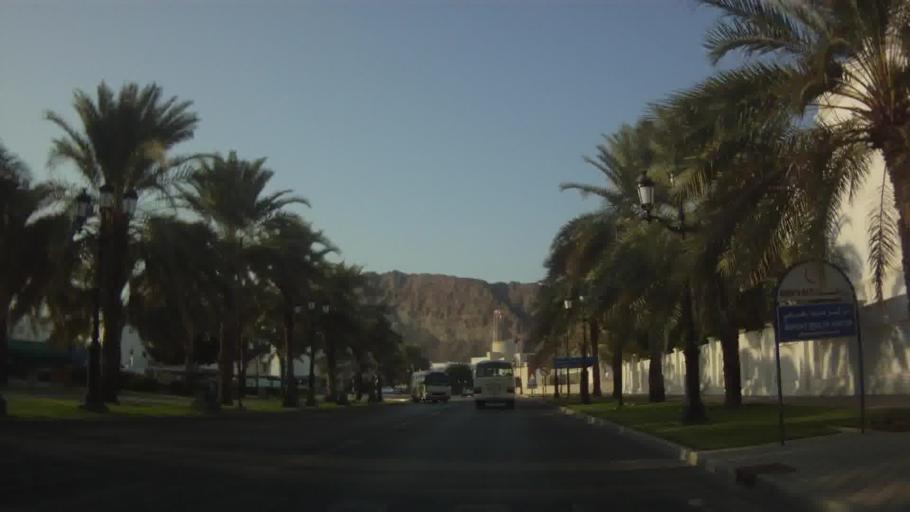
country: OM
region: Muhafazat Masqat
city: Muscat
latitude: 23.6134
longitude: 58.5914
